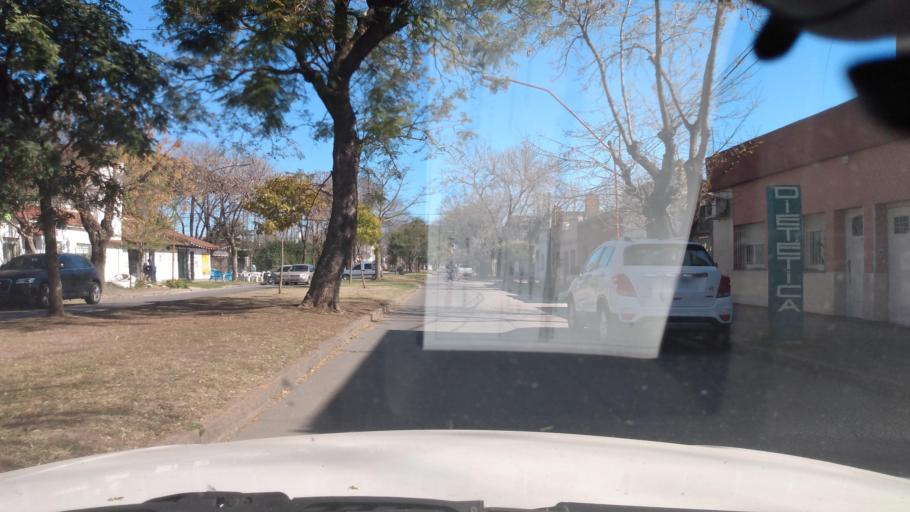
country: AR
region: Buenos Aires
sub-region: Partido de Mercedes
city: Mercedes
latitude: -34.6503
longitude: -59.4231
